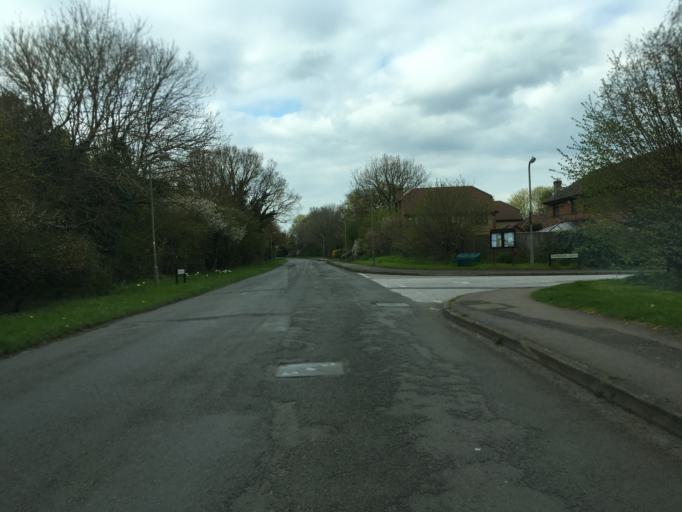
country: GB
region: England
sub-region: Oxfordshire
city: Bicester
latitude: 51.9213
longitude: -1.1490
